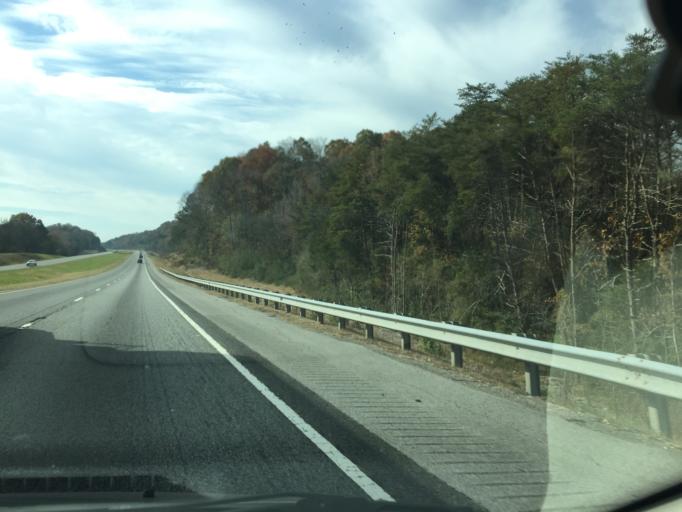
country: US
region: Georgia
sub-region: Dade County
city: Trenton
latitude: 34.9108
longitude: -85.4853
